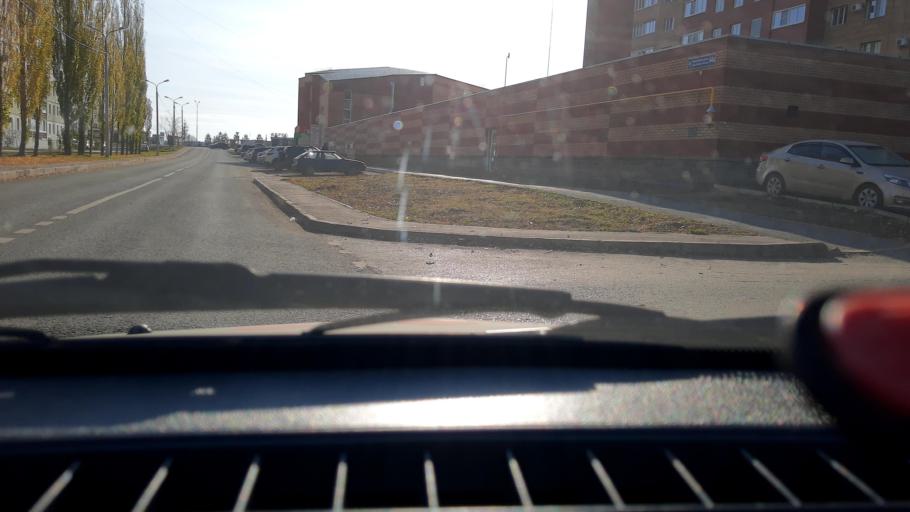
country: RU
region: Bashkortostan
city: Ufa
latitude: 54.7622
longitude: 56.0672
